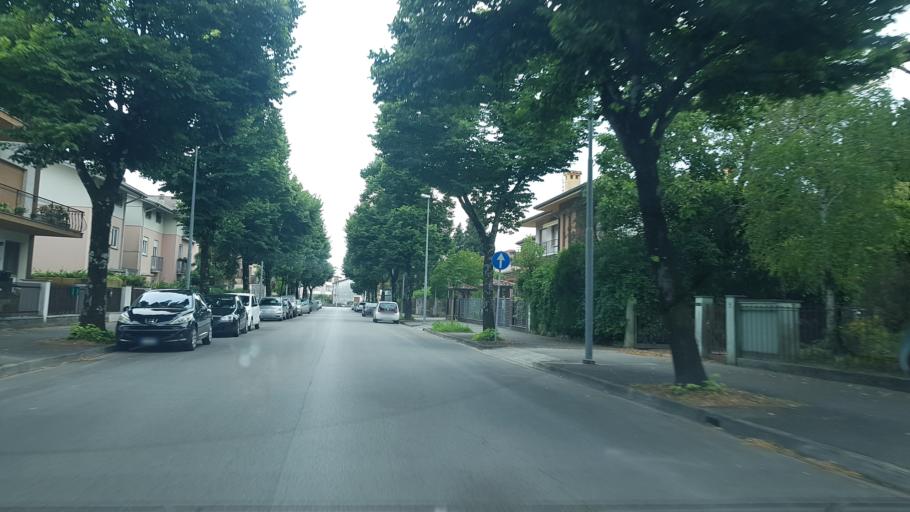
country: IT
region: Friuli Venezia Giulia
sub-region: Provincia di Gorizia
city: Gorizia
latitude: 45.9519
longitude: 13.6126
